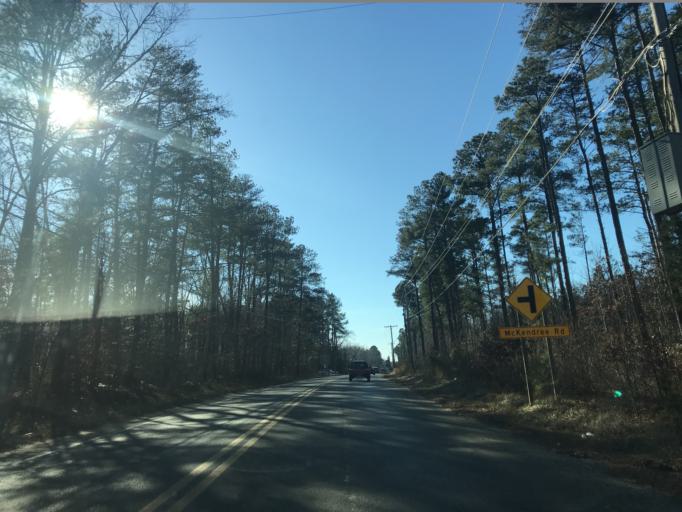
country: US
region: Maryland
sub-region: Prince George's County
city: Brandywine
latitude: 38.6881
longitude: -76.9046
